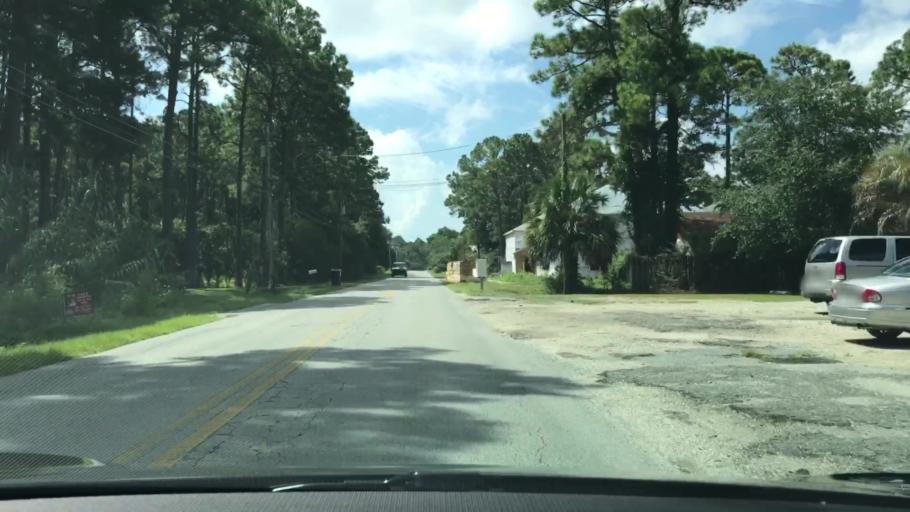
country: US
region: Florida
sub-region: Bay County
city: Panama City Beach
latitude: 30.1747
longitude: -85.7866
